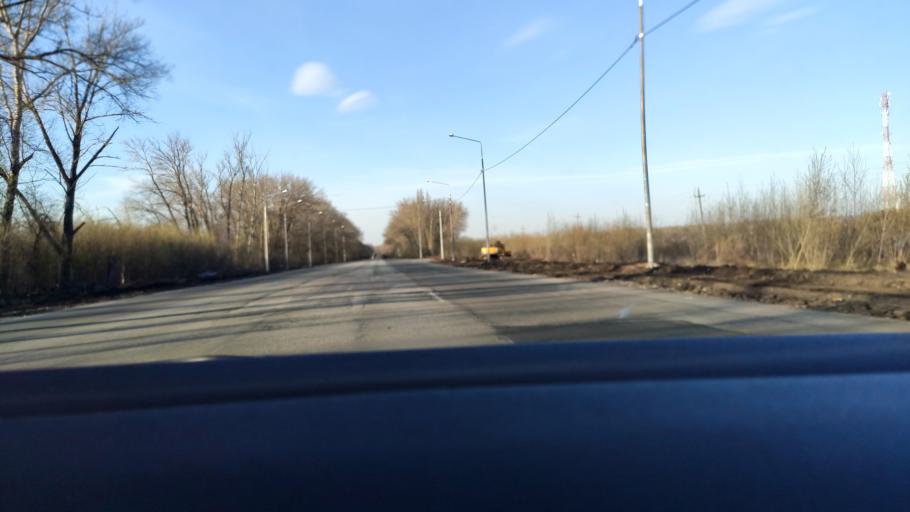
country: RU
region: Voronezj
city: Uryv-Pokrovka
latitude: 51.1722
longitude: 39.0761
